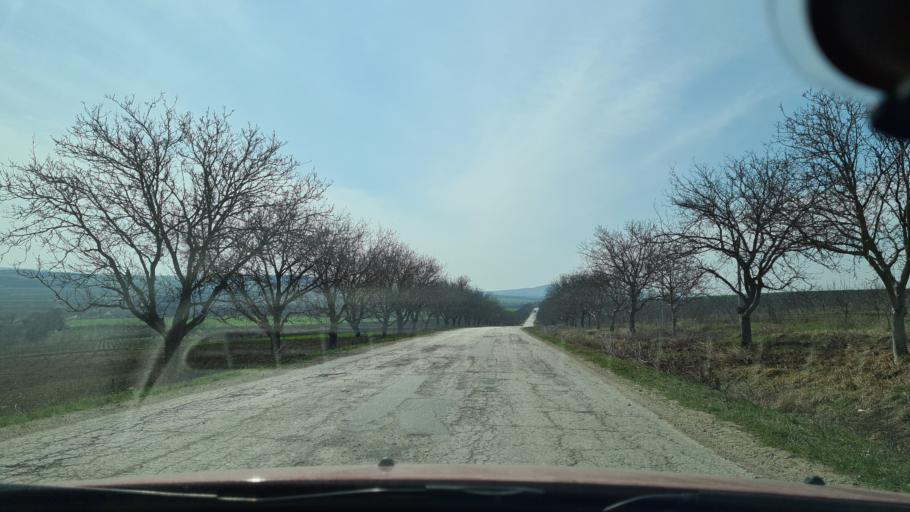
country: MD
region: Ungheni
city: Ungheni
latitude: 47.2859
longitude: 27.9232
